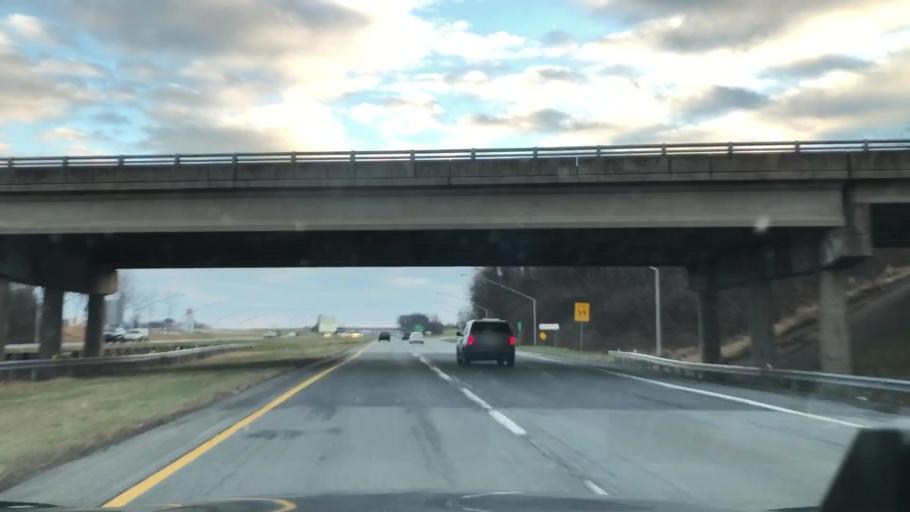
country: US
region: Pennsylvania
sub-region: Northampton County
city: Palmer Heights
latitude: 40.7044
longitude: -75.2900
